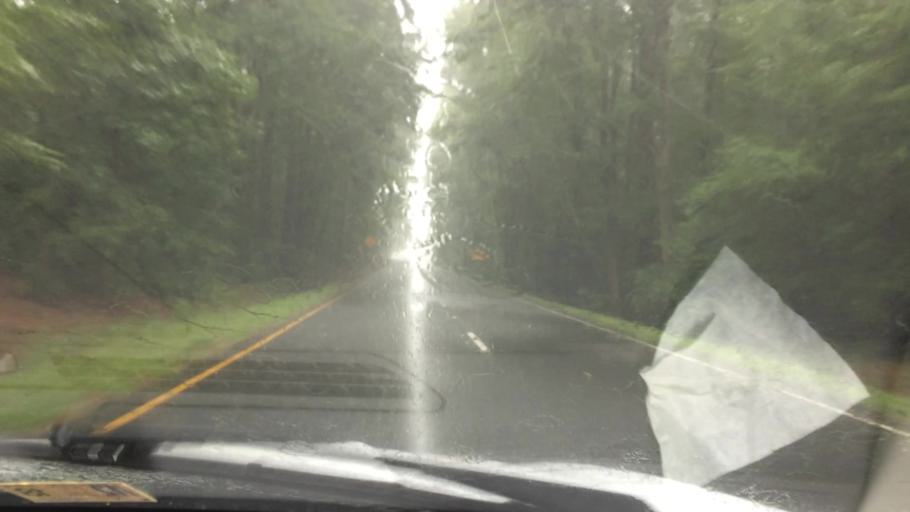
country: US
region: Virginia
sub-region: James City County
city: Williamsburg
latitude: 37.3933
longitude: -76.7760
